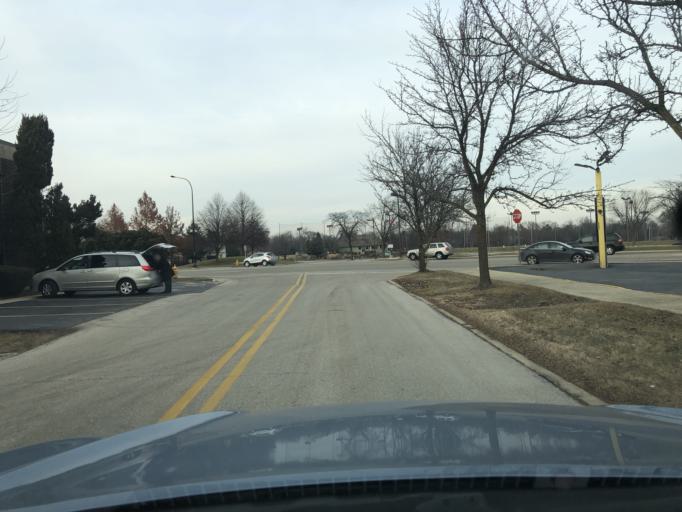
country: US
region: Illinois
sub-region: DuPage County
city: Addison
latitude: 41.9415
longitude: -88.0118
